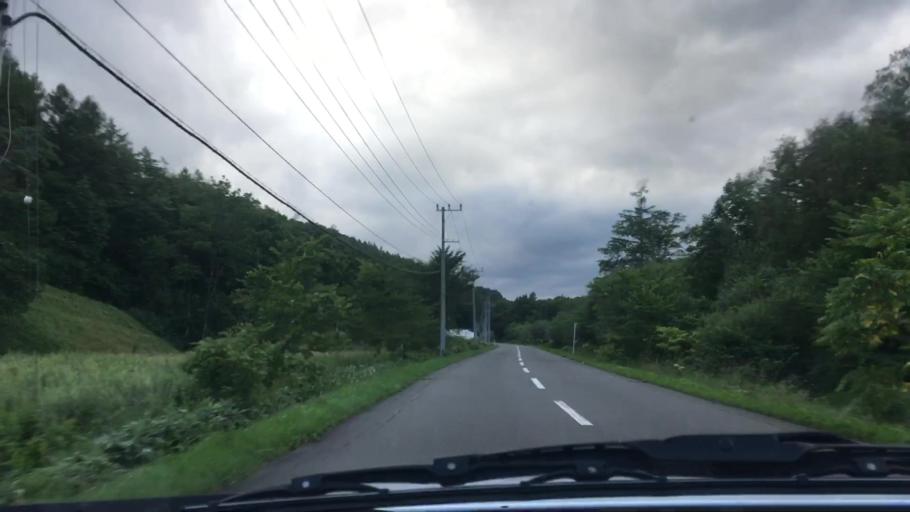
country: JP
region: Hokkaido
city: Otofuke
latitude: 43.1422
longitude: 142.8833
